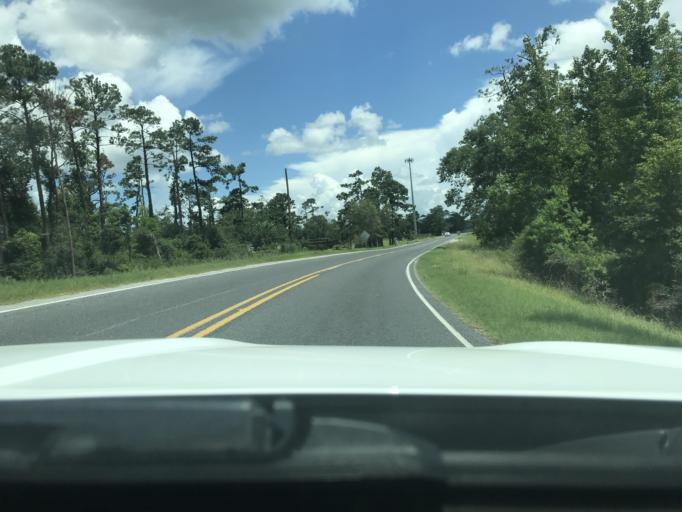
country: US
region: Louisiana
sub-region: Calcasieu Parish
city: Moss Bluff
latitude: 30.2770
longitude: -93.1817
